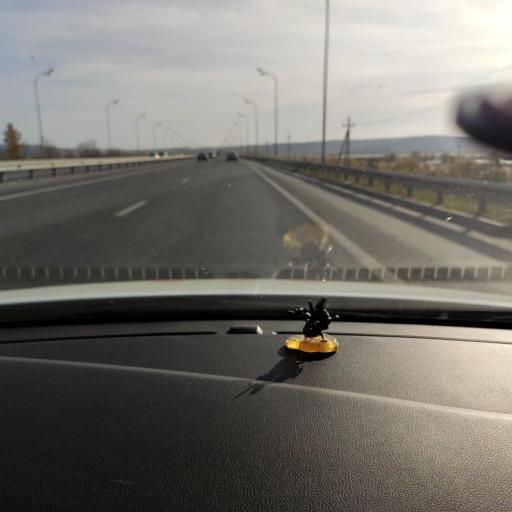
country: RU
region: Tatarstan
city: Osinovo
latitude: 55.8136
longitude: 48.8421
